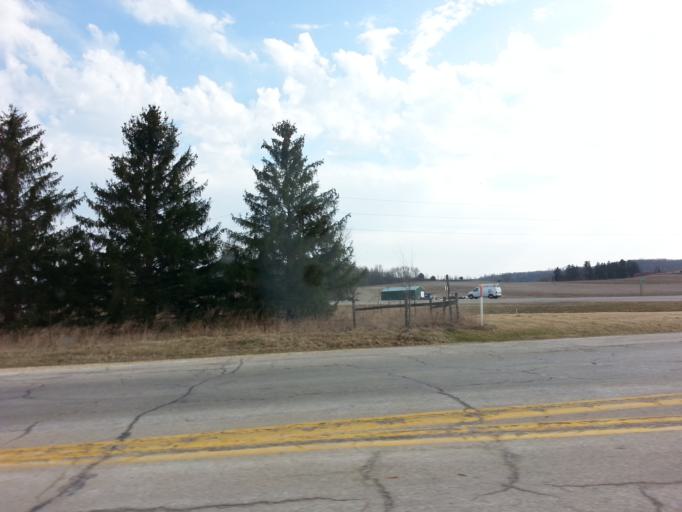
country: US
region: Wisconsin
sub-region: Pierce County
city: Ellsworth
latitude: 44.7325
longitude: -92.4512
